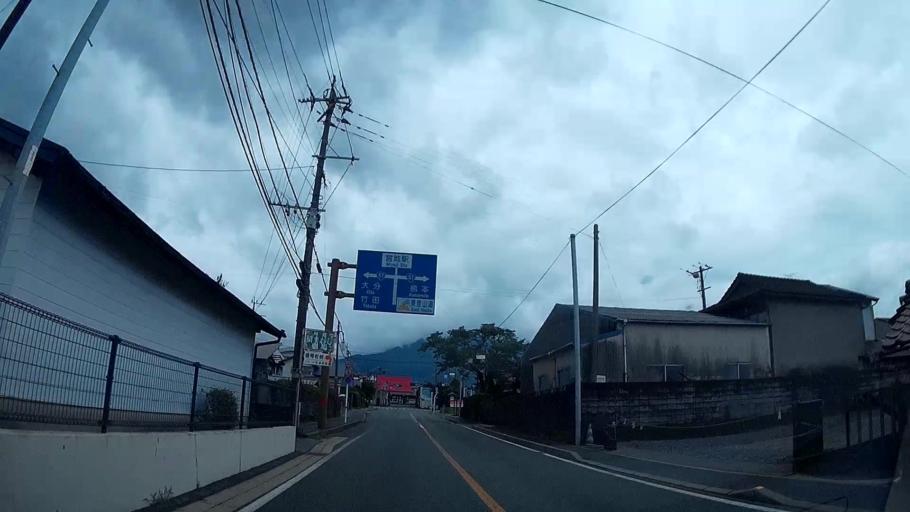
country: JP
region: Kumamoto
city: Aso
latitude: 32.9390
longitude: 131.1175
